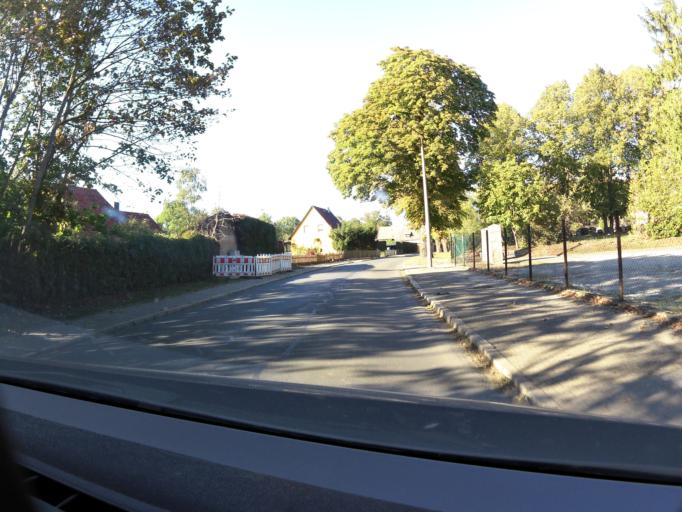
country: DE
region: Saxony-Anhalt
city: Wegeleben
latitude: 51.8899
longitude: 11.1857
